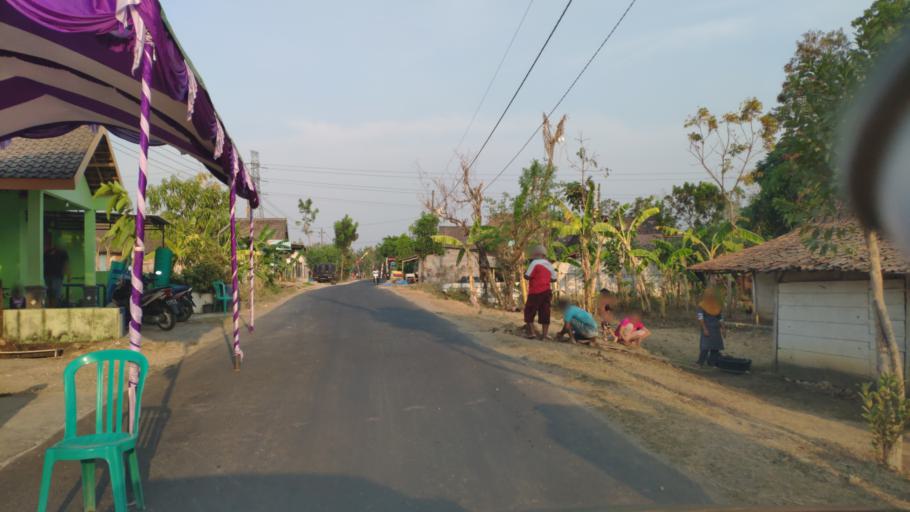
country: ID
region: Central Java
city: Kunden
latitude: -6.9532
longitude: 111.4013
